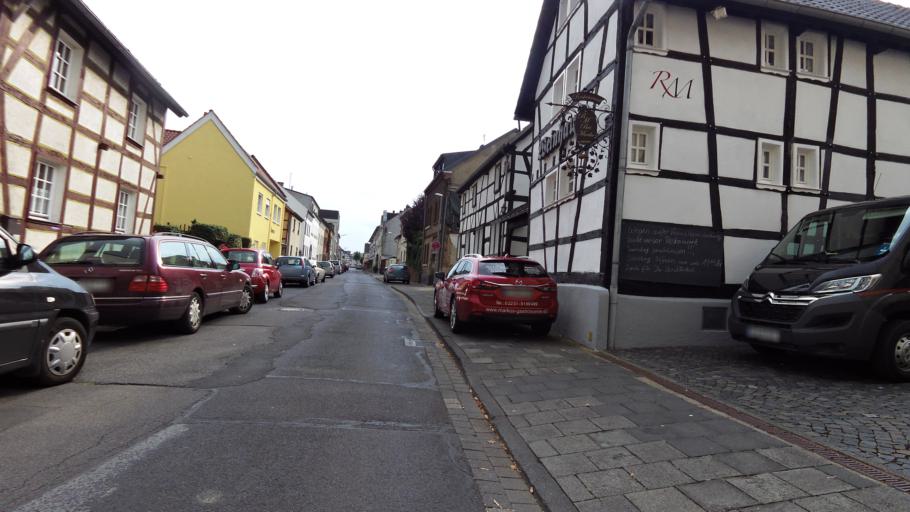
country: DE
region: North Rhine-Westphalia
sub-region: Regierungsbezirk Koln
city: Euskirchen
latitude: 50.6516
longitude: 6.8305
